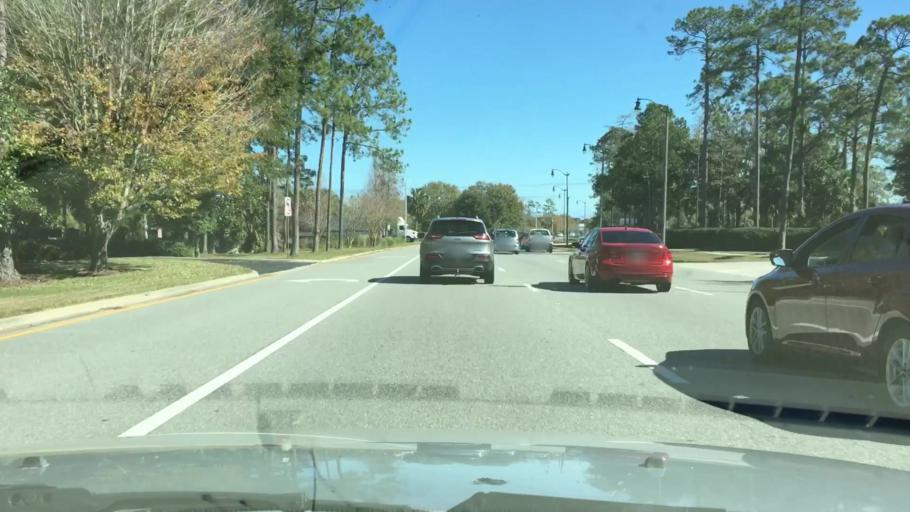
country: US
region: Florida
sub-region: Flagler County
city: Palm Coast
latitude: 29.5525
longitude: -81.2313
